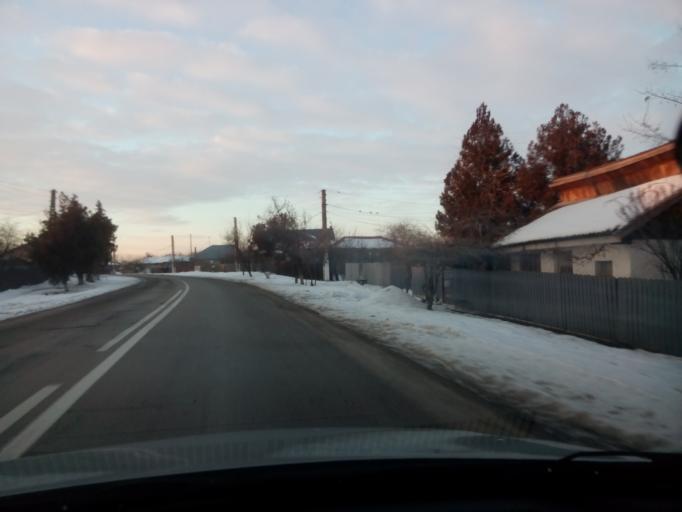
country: RO
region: Calarasi
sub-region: Comuna Soldanu
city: Negoesti
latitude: 44.2284
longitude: 26.5073
